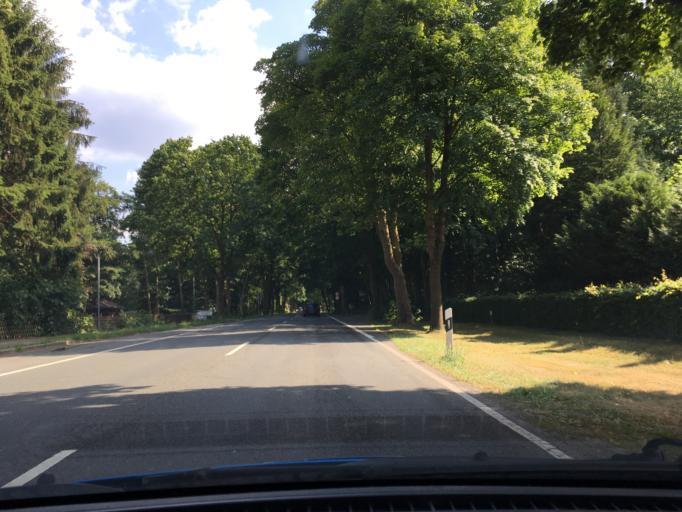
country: DE
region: Lower Saxony
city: Welle
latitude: 53.2323
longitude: 9.8044
